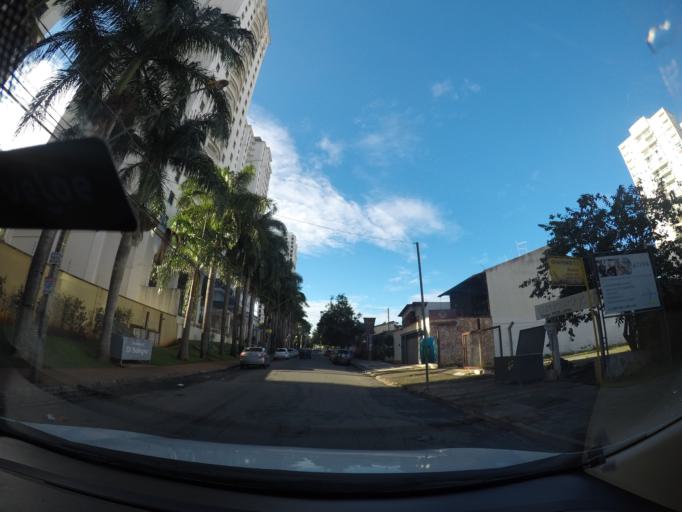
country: BR
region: Goias
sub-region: Goiania
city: Goiania
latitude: -16.7179
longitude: -49.2691
